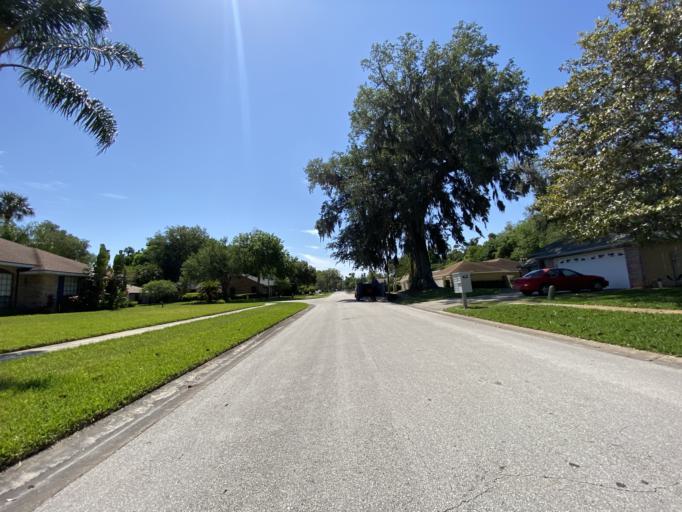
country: US
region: Florida
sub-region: Volusia County
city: South Daytona
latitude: 29.1542
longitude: -81.0144
